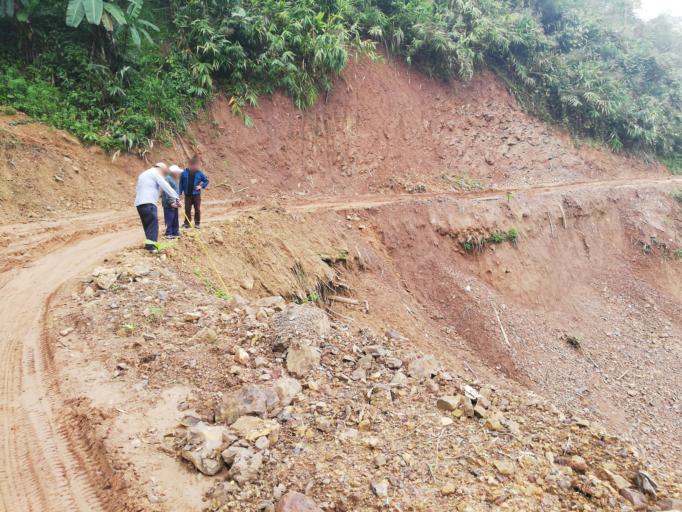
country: LA
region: Loungnamtha
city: Louang Namtha
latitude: 20.8643
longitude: 101.4982
